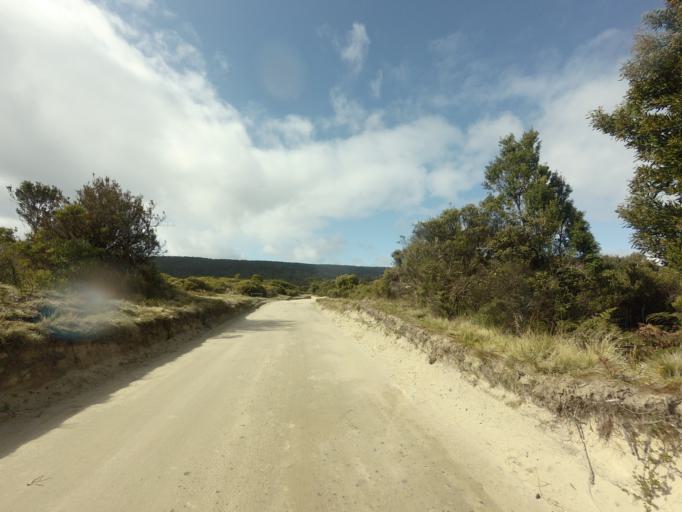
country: AU
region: Tasmania
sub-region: Huon Valley
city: Geeveston
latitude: -43.5798
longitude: 146.8876
